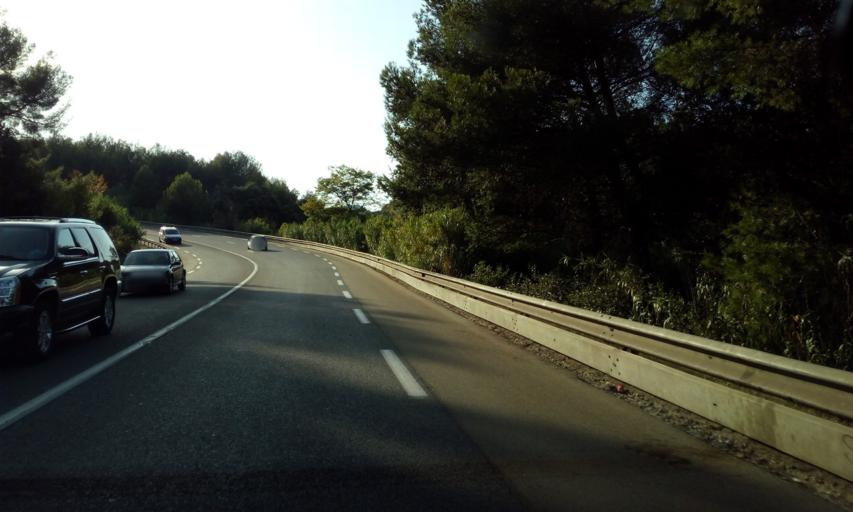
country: FR
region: Provence-Alpes-Cote d'Azur
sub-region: Departement du Var
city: Bandol
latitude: 43.1497
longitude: 5.7612
